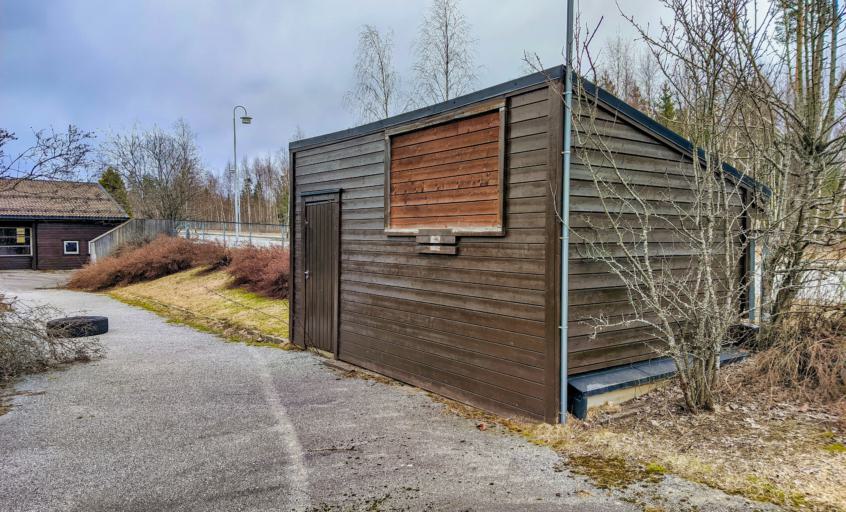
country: NO
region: Akershus
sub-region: Ullensaker
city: Jessheim
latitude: 60.1652
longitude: 11.1453
